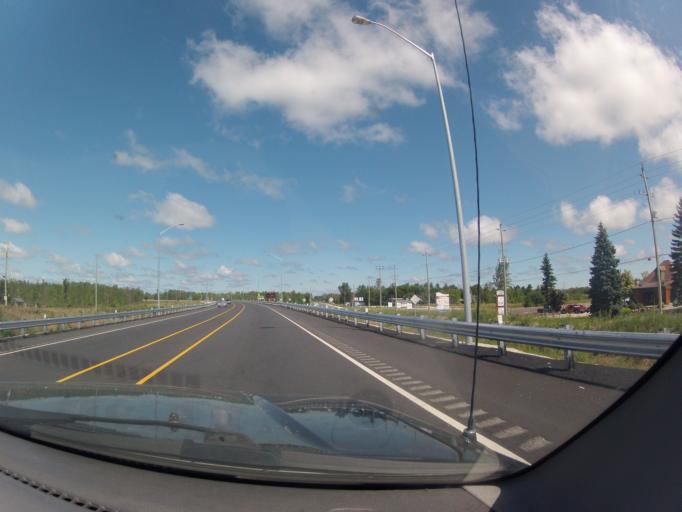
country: CA
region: Ontario
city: Wasaga Beach
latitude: 44.4566
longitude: -80.1046
